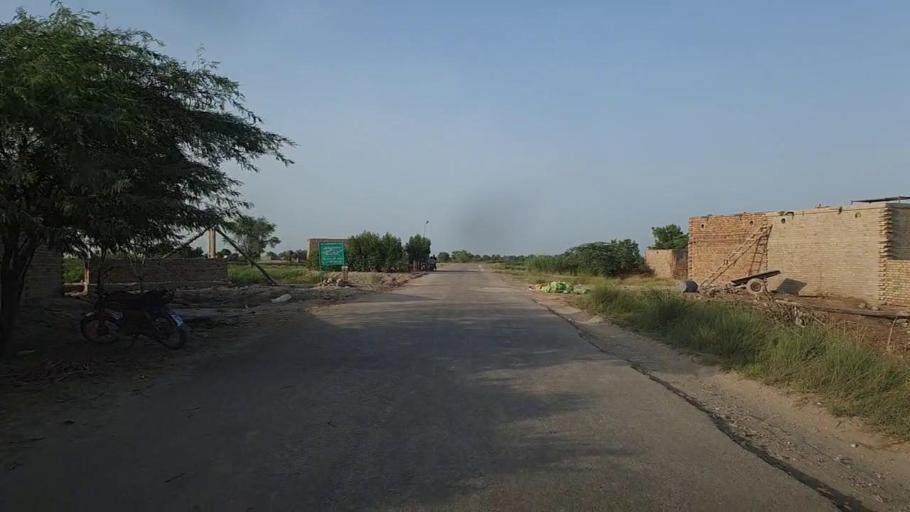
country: PK
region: Sindh
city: Ubauro
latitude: 28.1053
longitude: 69.8146
